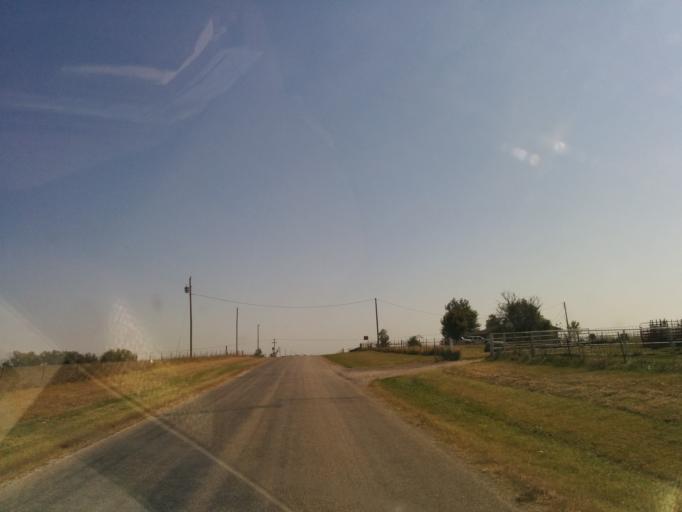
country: US
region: Oklahoma
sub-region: Okmulgee County
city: Beggs
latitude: 35.7991
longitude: -96.0894
